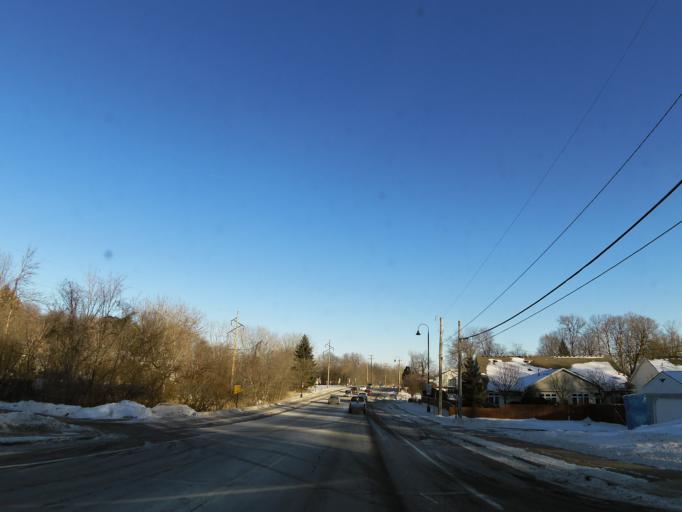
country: US
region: Minnesota
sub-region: Hennepin County
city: Mound
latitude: 44.9369
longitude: -93.6502
